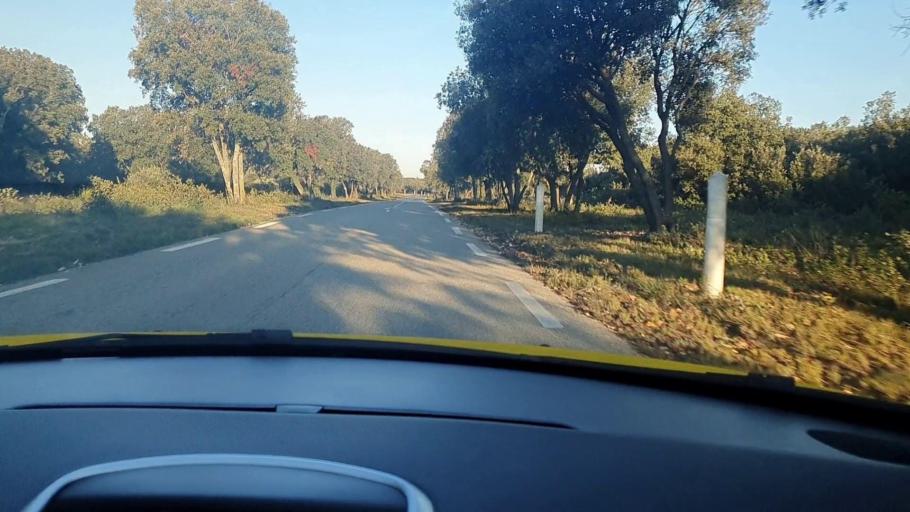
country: FR
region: Languedoc-Roussillon
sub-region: Departement du Gard
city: Montaren-et-Saint-Mediers
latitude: 44.1009
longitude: 4.3874
